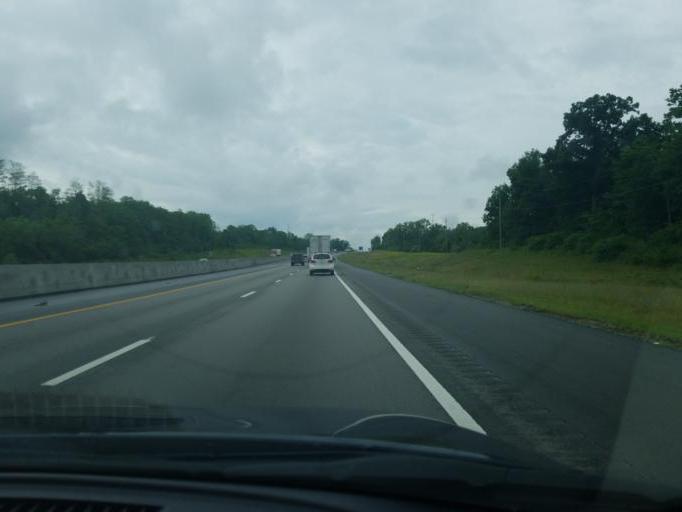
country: US
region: Ohio
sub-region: Warren County
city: Morrow
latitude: 39.4182
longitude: -84.1082
